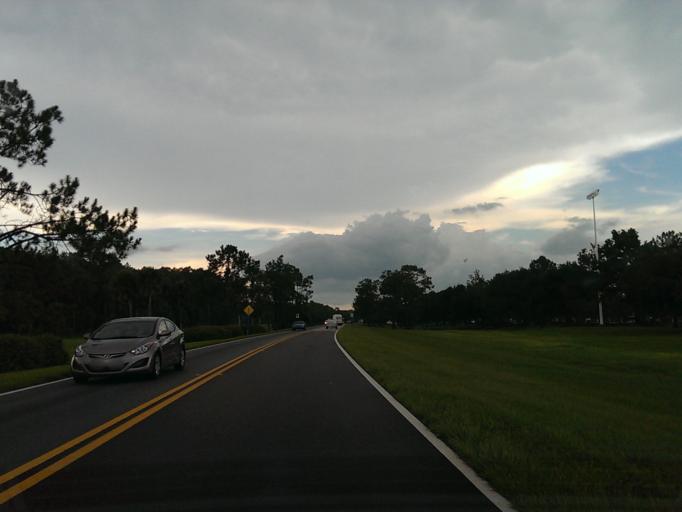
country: US
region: Florida
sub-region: Osceola County
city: Celebration
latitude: 28.3967
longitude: -81.5819
